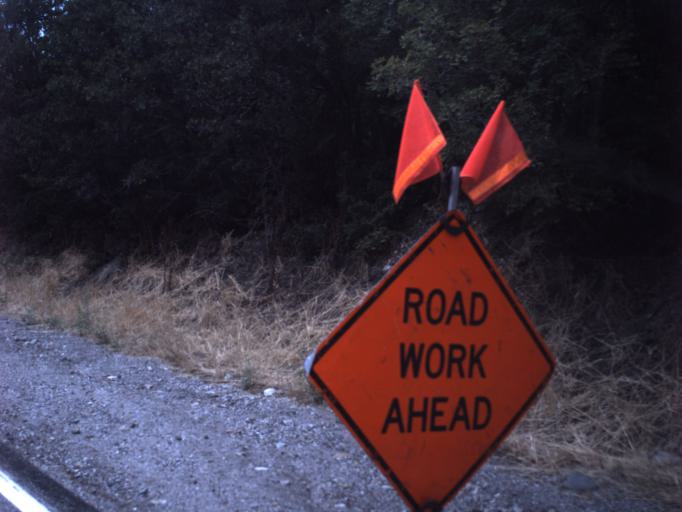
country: US
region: Utah
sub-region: Salt Lake County
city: Granite
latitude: 40.5718
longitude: -111.7718
